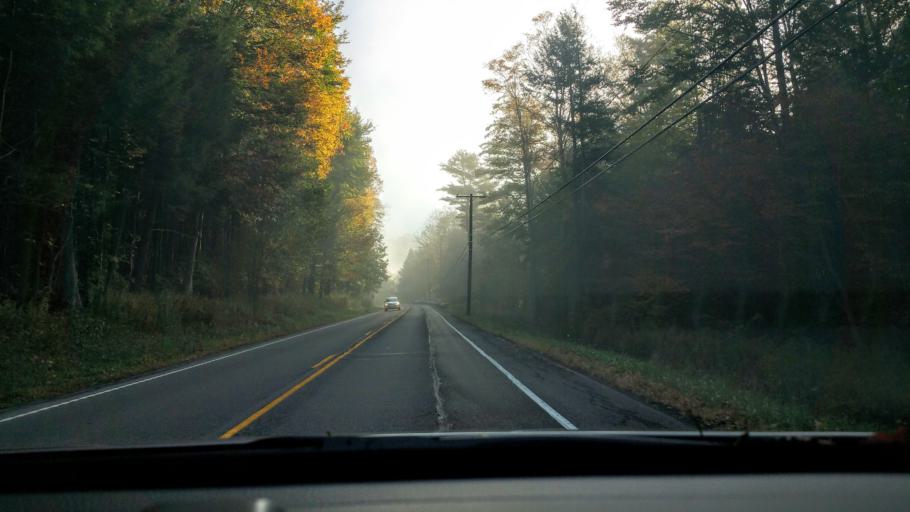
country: US
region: Pennsylvania
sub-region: Clearfield County
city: Treasure Lake
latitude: 41.1833
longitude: -78.6099
